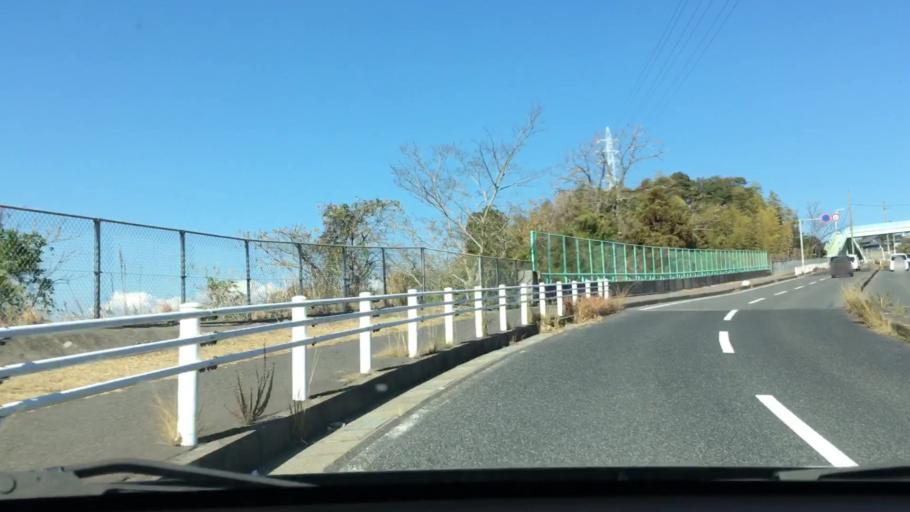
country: JP
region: Kagoshima
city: Kagoshima-shi
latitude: 31.5561
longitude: 130.5263
